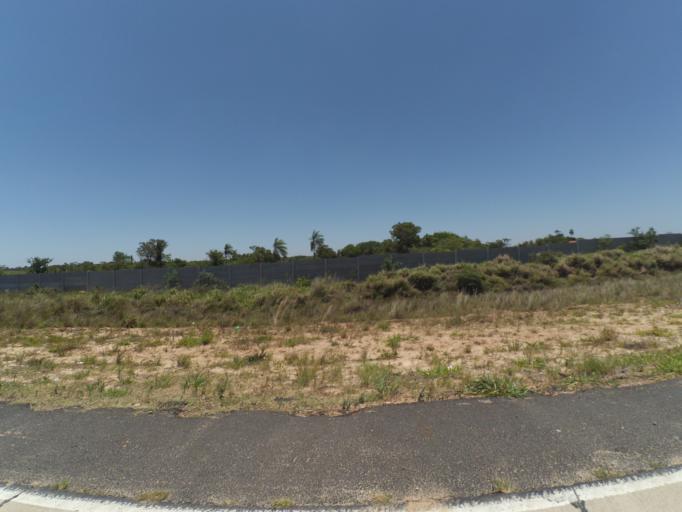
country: BO
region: Santa Cruz
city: Santa Cruz de la Sierra
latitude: -17.7881
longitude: -63.2736
